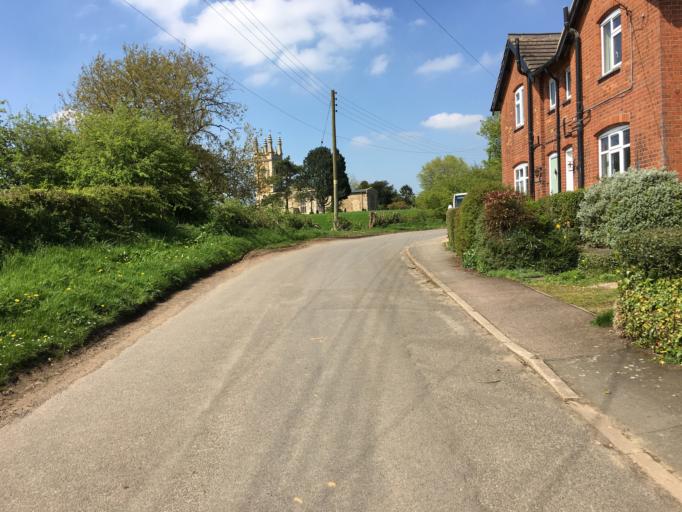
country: GB
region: England
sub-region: Leicestershire
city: Houghton on the Hill
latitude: 52.6018
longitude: -0.9743
